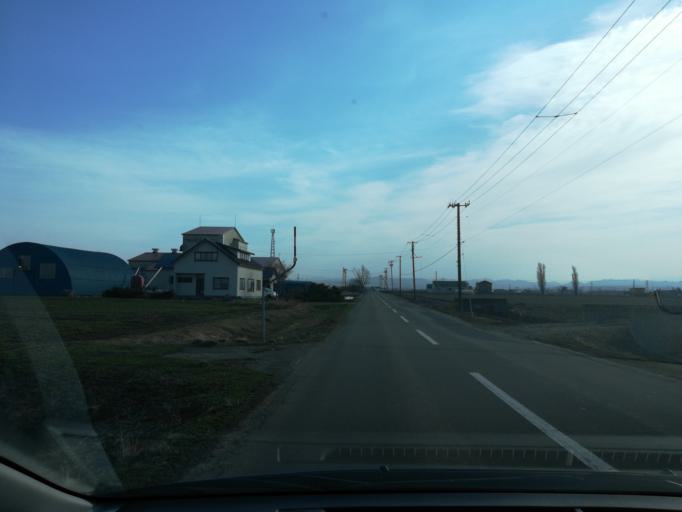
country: JP
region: Hokkaido
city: Iwamizawa
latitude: 43.1934
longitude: 141.7129
